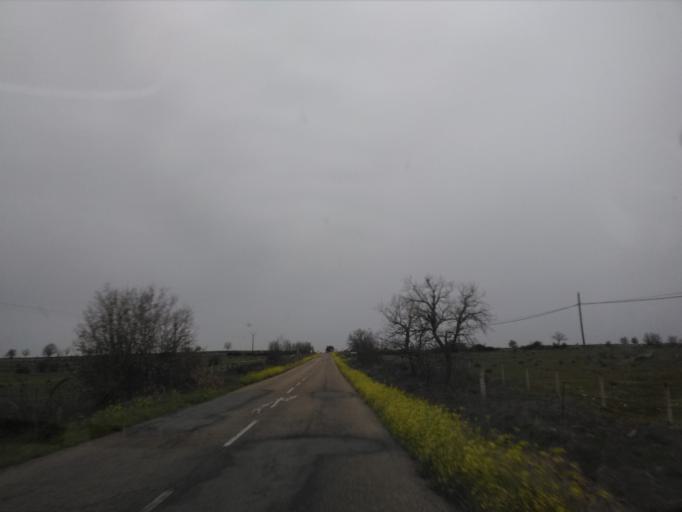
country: ES
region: Castille and Leon
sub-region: Provincia de Salamanca
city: Moronta
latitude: 40.9840
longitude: -6.4623
